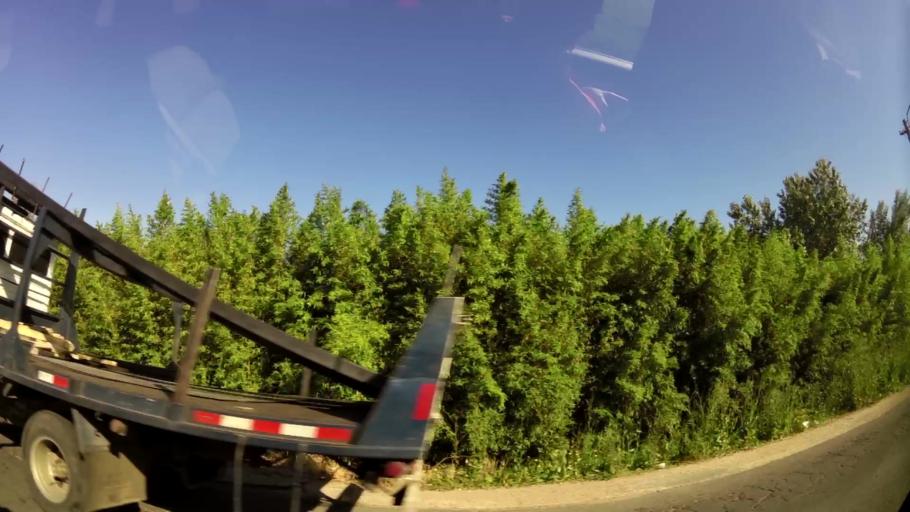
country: UY
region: Canelones
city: La Paz
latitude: -34.8158
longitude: -56.1715
